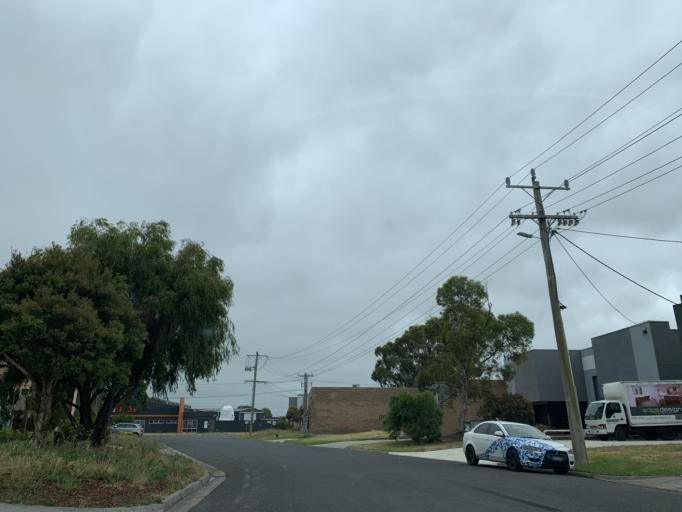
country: AU
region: Victoria
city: Heatherton
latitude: -37.9919
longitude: 145.1088
